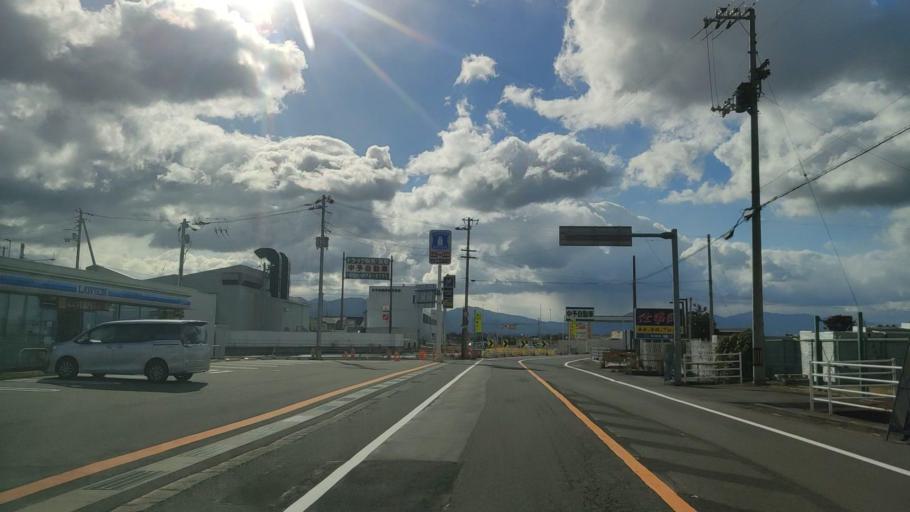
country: JP
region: Ehime
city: Masaki-cho
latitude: 33.8218
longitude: 132.7133
